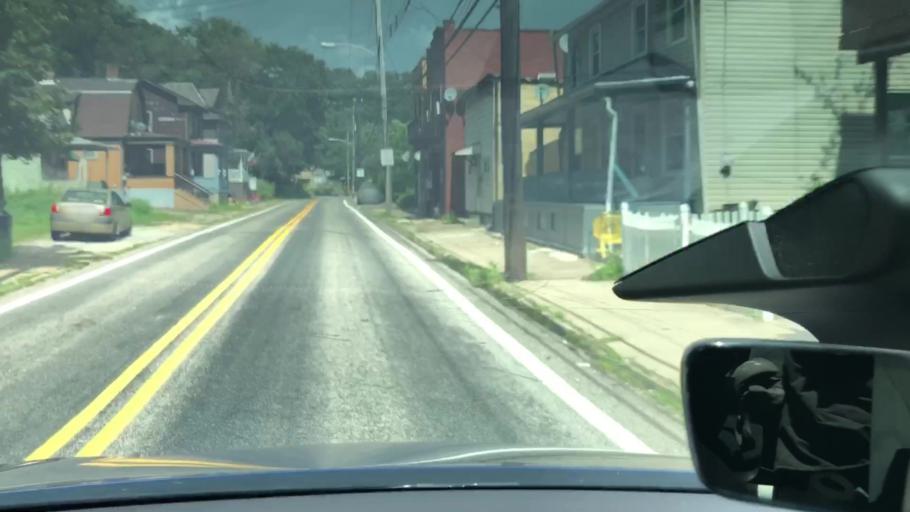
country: US
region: Pennsylvania
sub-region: Allegheny County
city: Turtle Creek
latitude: 40.4119
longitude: -79.8255
